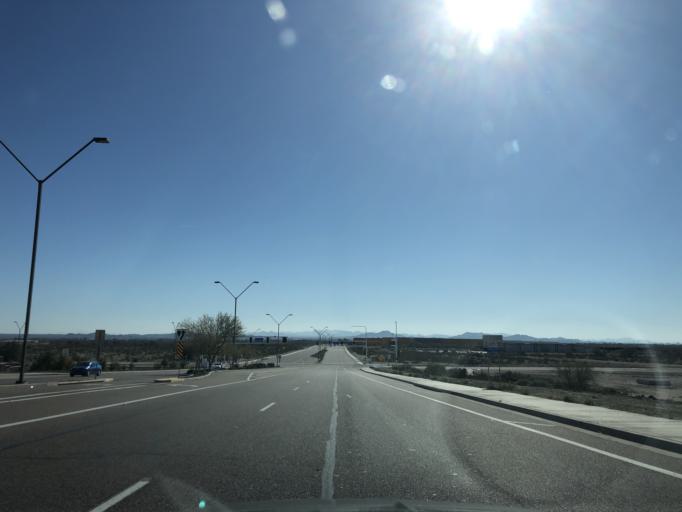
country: US
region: Arizona
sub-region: Maricopa County
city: Citrus Park
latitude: 33.4591
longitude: -112.5044
